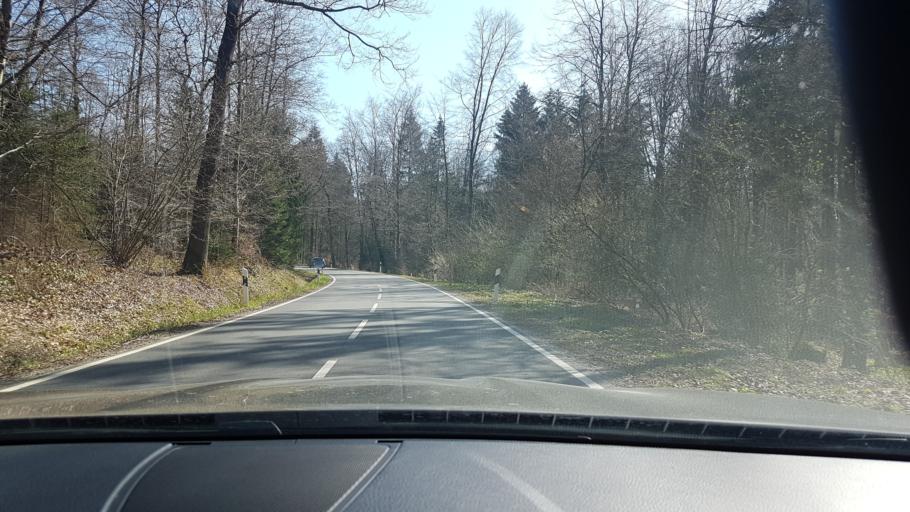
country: DE
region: Lower Saxony
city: Coppenbrugge
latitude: 52.1443
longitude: 9.5789
